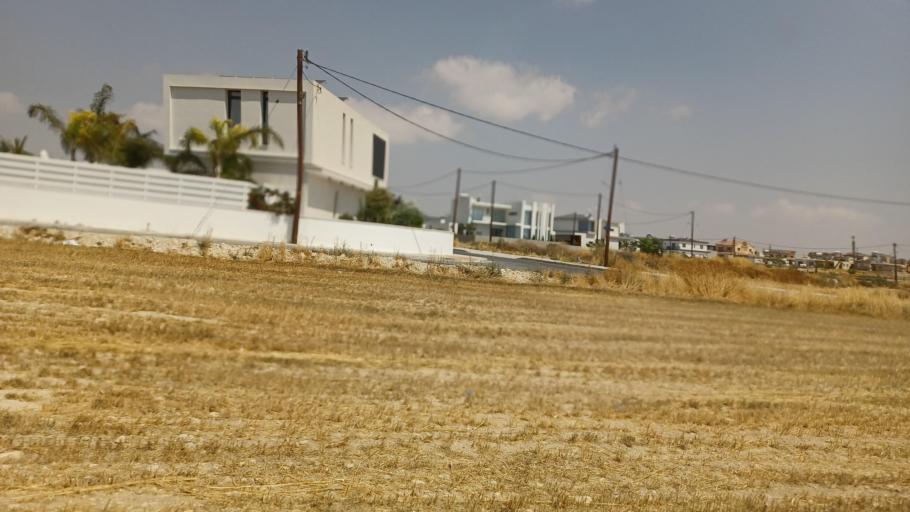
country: CY
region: Larnaka
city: Aradippou
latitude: 34.9385
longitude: 33.6068
